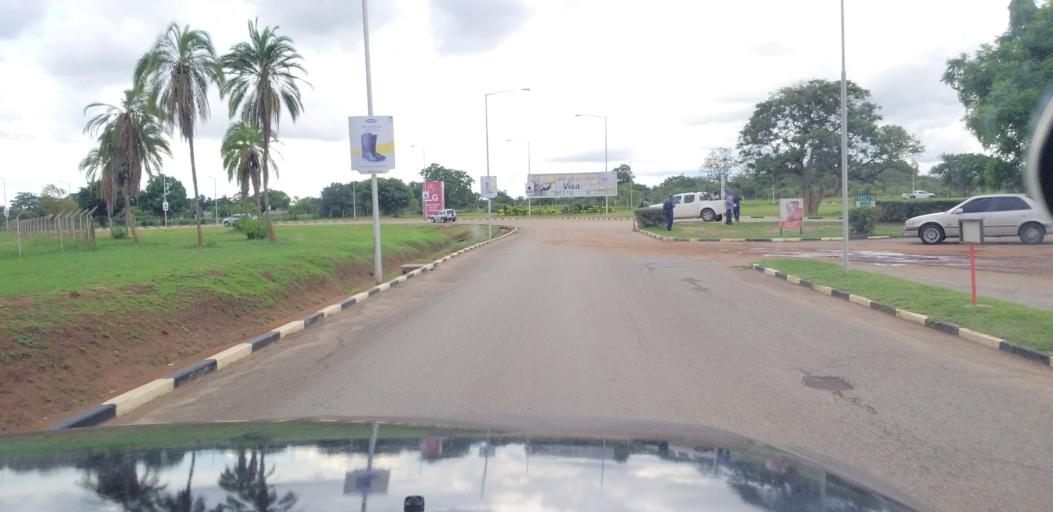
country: ZM
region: Lusaka
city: Lusaka
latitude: -15.3218
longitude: 28.4455
